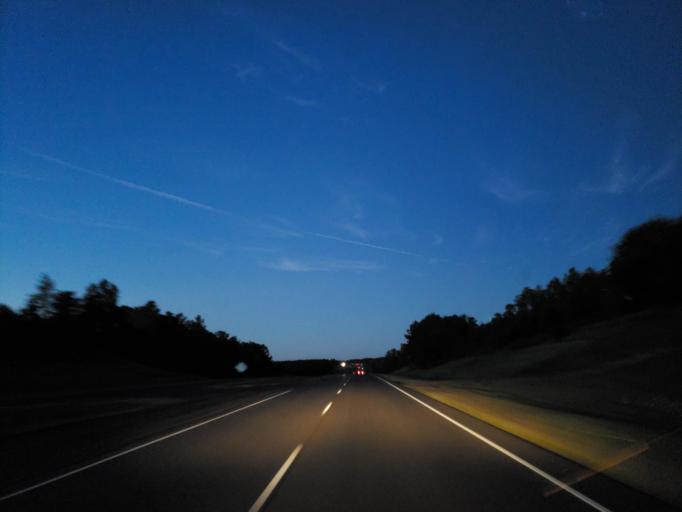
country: US
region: Mississippi
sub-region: Clarke County
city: Quitman
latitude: 32.0270
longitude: -88.6847
